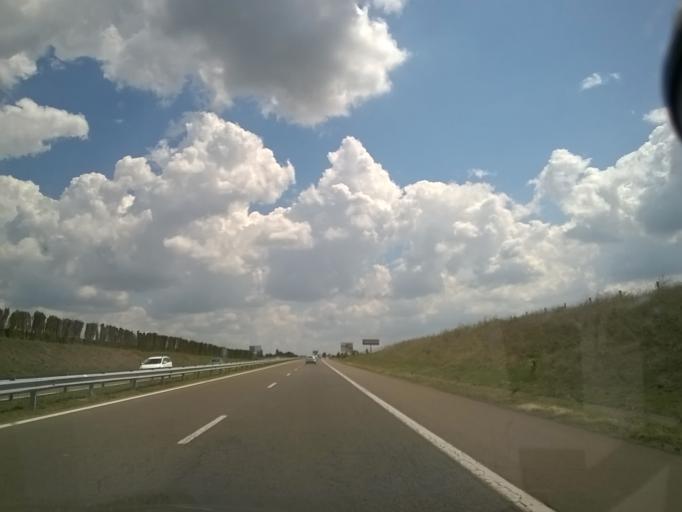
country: BG
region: Burgas
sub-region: Obshtina Karnobat
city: Karnobat
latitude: 42.5901
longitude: 27.0492
